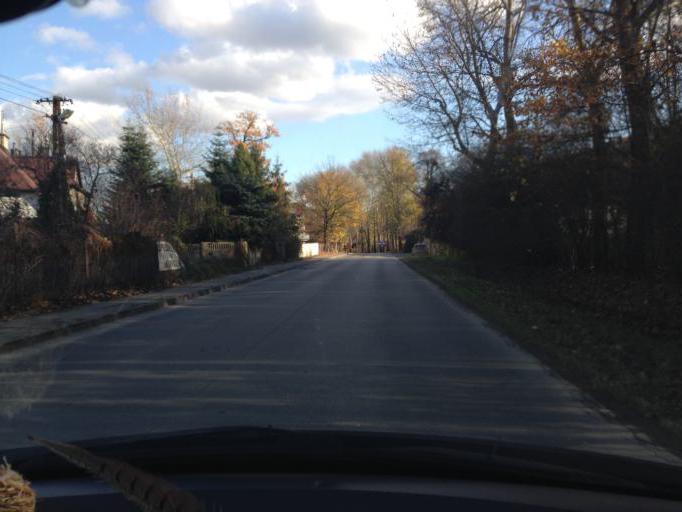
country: PL
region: Lesser Poland Voivodeship
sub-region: Powiat krakowski
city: Rzaska
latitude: 50.0683
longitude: 19.8423
